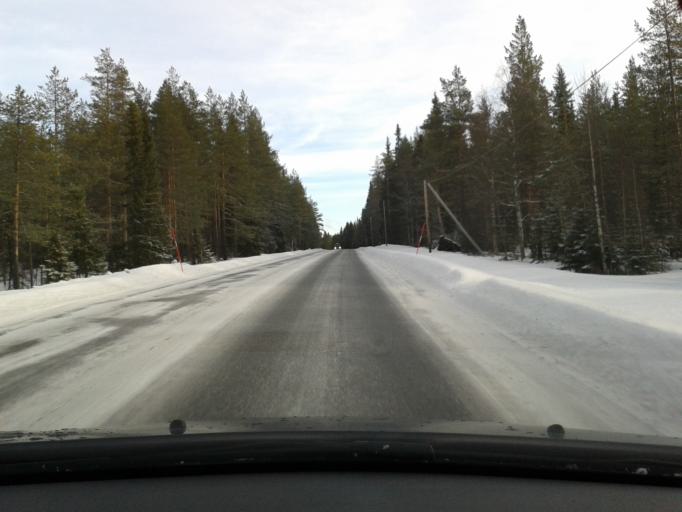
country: SE
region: Vaesterbotten
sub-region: Vilhelmina Kommun
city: Vilhelmina
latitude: 64.6470
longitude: 16.5444
